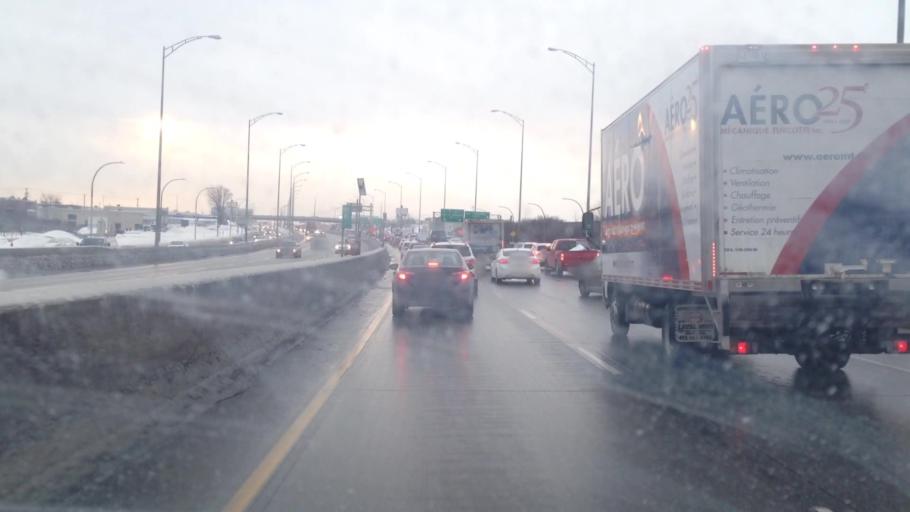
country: CA
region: Quebec
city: Dorval
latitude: 45.5022
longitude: -73.7552
